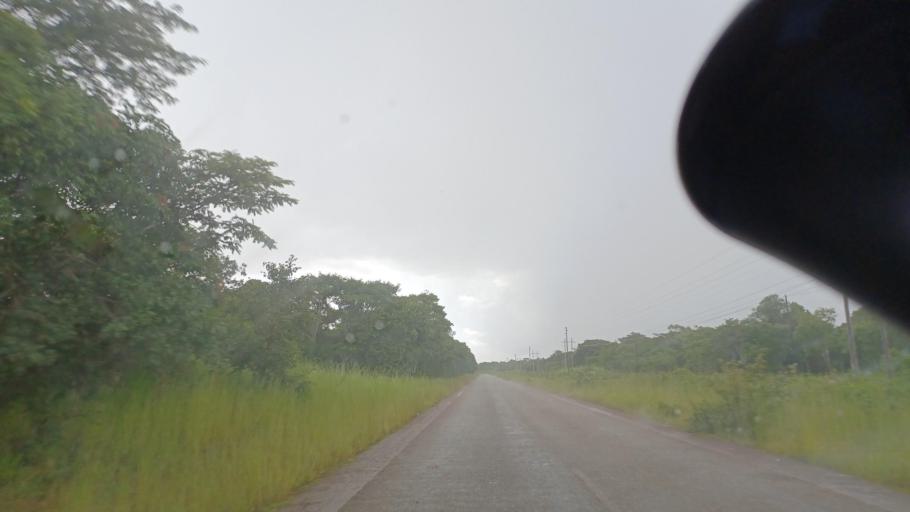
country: ZM
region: North-Western
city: Kasempa
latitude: -13.0916
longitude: 25.9314
